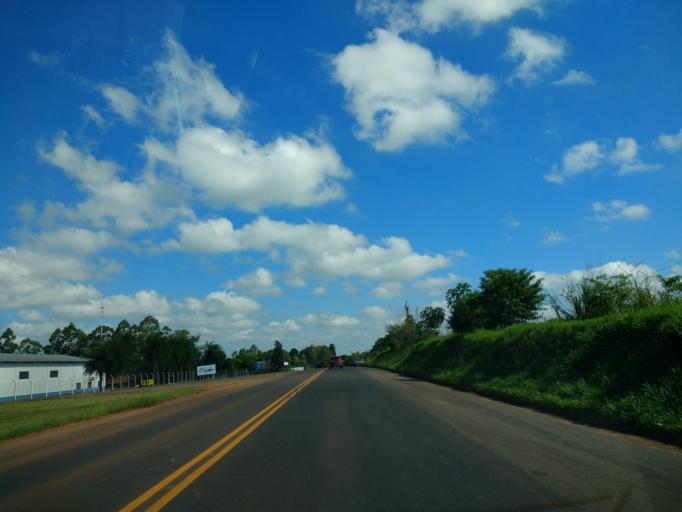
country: BR
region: Parana
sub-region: Umuarama
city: Umuarama
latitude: -23.8325
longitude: -53.3551
